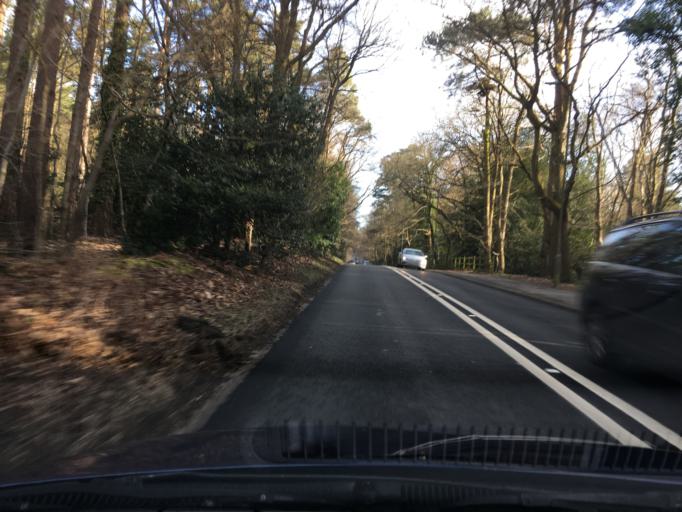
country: GB
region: England
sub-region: Bracknell Forest
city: Crowthorne
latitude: 51.3576
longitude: -0.7985
